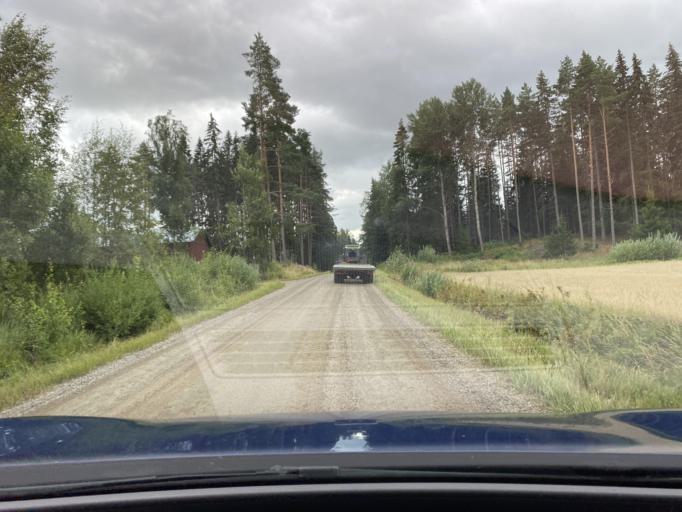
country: FI
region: Pirkanmaa
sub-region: Lounais-Pirkanmaa
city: Punkalaidun
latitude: 61.1785
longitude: 23.1821
